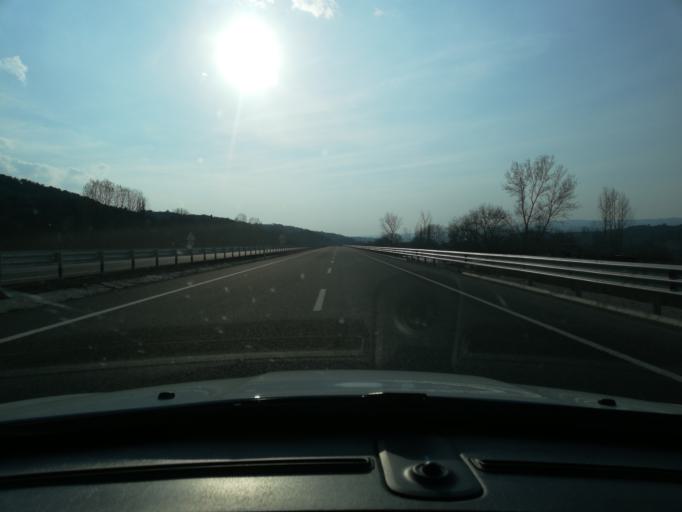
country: TR
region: Kastamonu
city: Igdir
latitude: 41.2270
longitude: 33.1257
